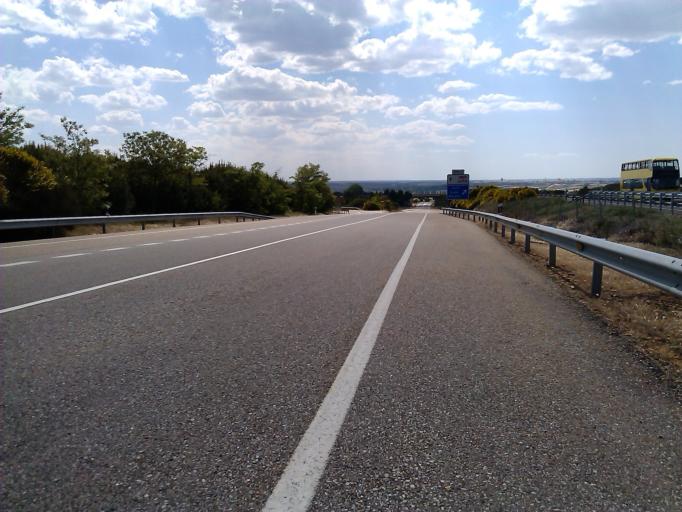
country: ES
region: Castille and Leon
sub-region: Provincia de Palencia
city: Moratinos
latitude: 42.3660
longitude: -4.9734
